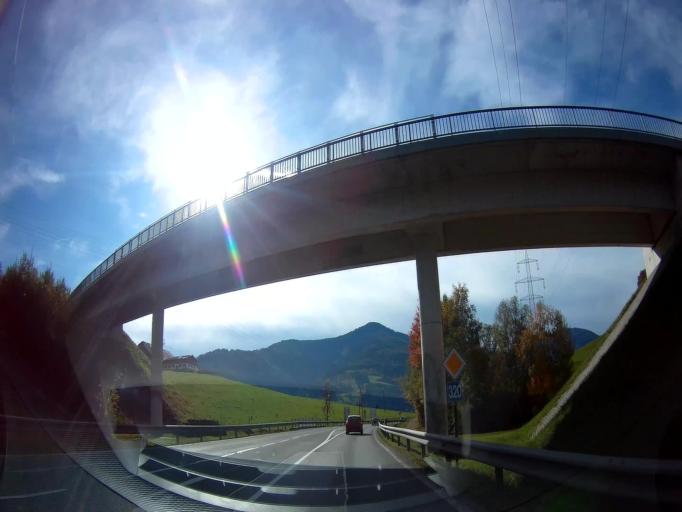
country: AT
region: Styria
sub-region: Politischer Bezirk Liezen
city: Grobming
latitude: 47.4454
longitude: 13.9131
